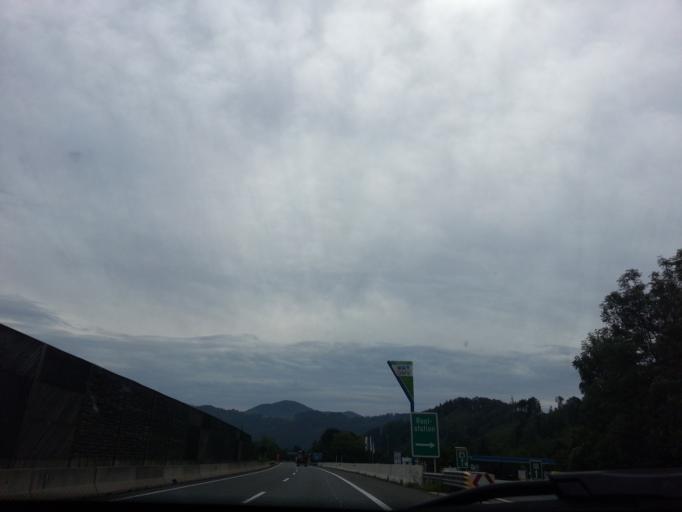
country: AT
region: Styria
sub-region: Politischer Bezirk Graz-Umgebung
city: Deutschfeistritz
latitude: 47.2068
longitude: 15.3142
